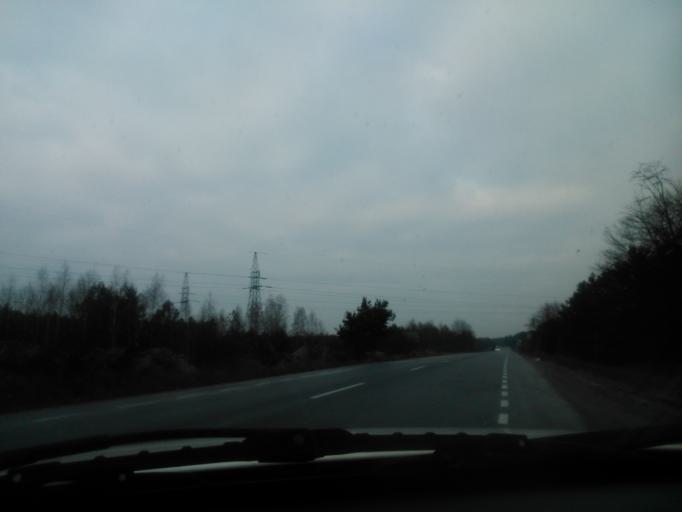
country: PL
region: Kujawsko-Pomorskie
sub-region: Powiat torunski
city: Lysomice
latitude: 53.0495
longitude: 18.6169
